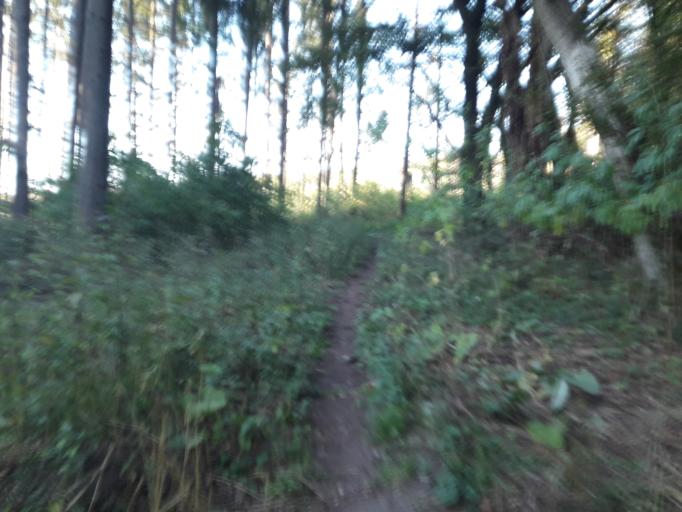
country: DE
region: North Rhine-Westphalia
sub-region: Regierungsbezirk Detmold
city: Schlangen
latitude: 51.7858
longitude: 8.8788
